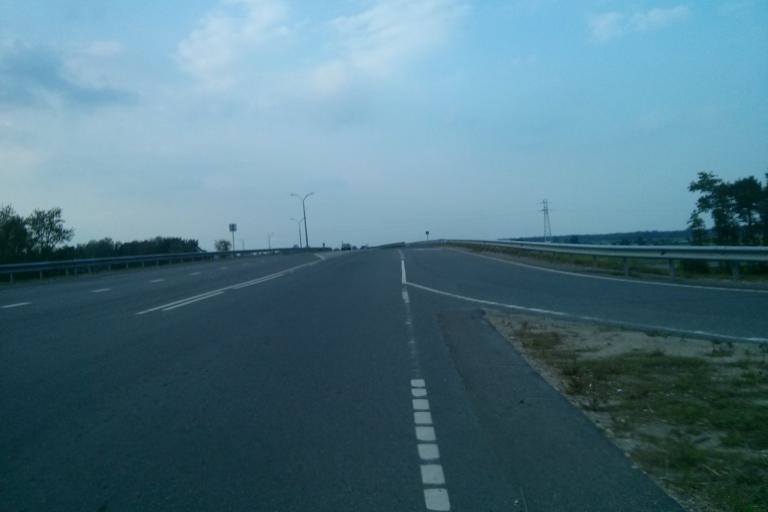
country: BY
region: Minsk
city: Chervyen'
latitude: 53.7225
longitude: 28.3950
